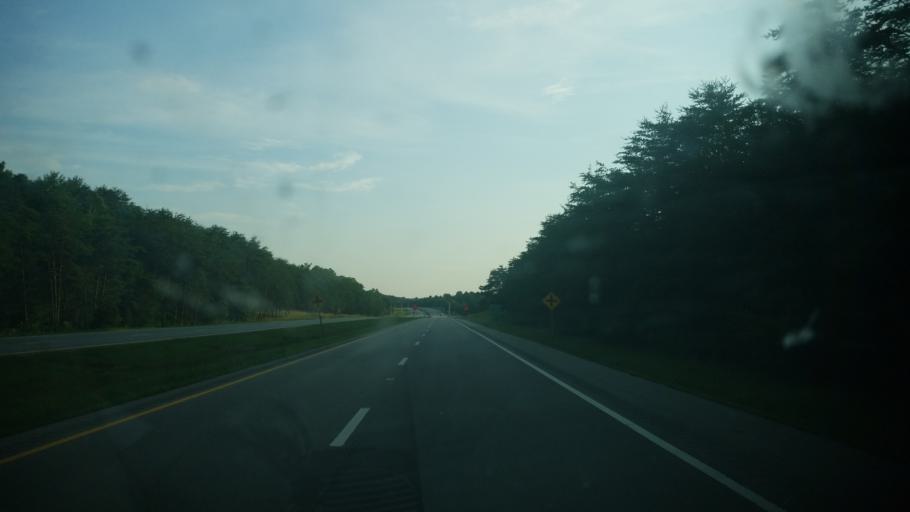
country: US
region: Ohio
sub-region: Adams County
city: Peebles
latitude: 38.9778
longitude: -83.3338
